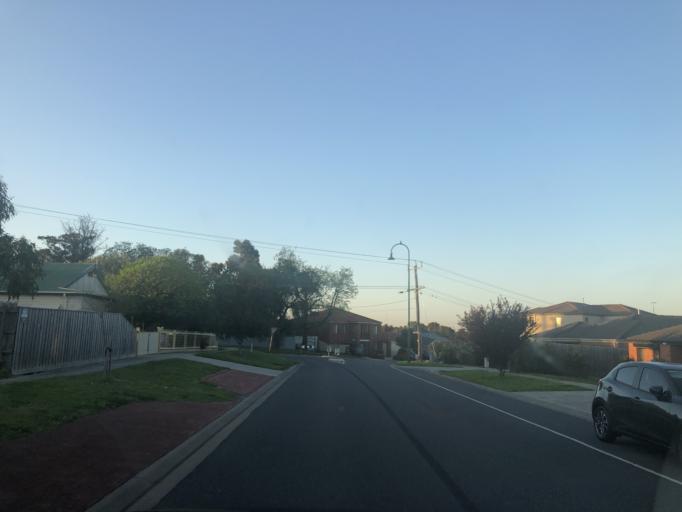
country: AU
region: Victoria
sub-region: Casey
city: Lynbrook
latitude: -38.0448
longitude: 145.2593
